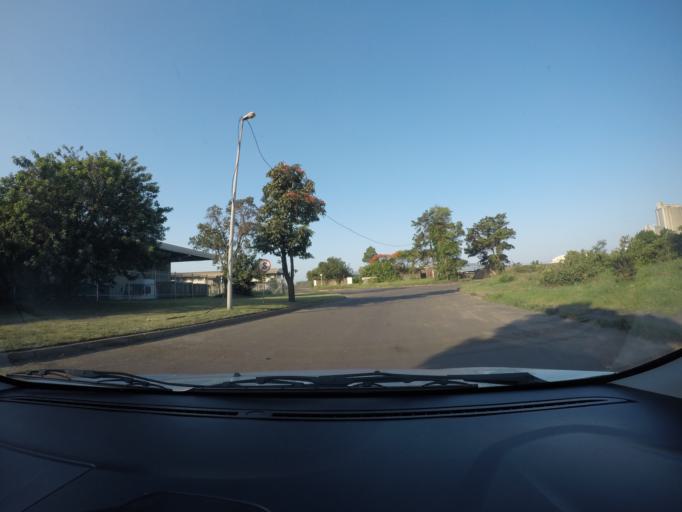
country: ZA
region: KwaZulu-Natal
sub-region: uThungulu District Municipality
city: Richards Bay
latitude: -28.7577
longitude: 32.0095
